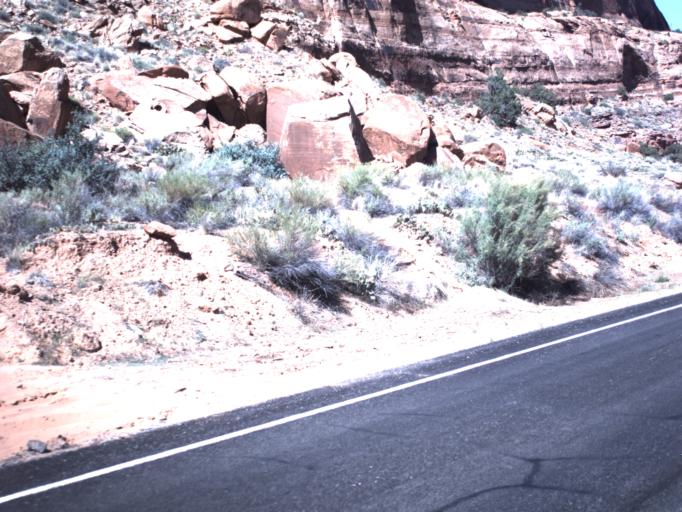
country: US
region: Utah
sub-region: Grand County
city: Moab
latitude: 38.5583
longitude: -109.5882
